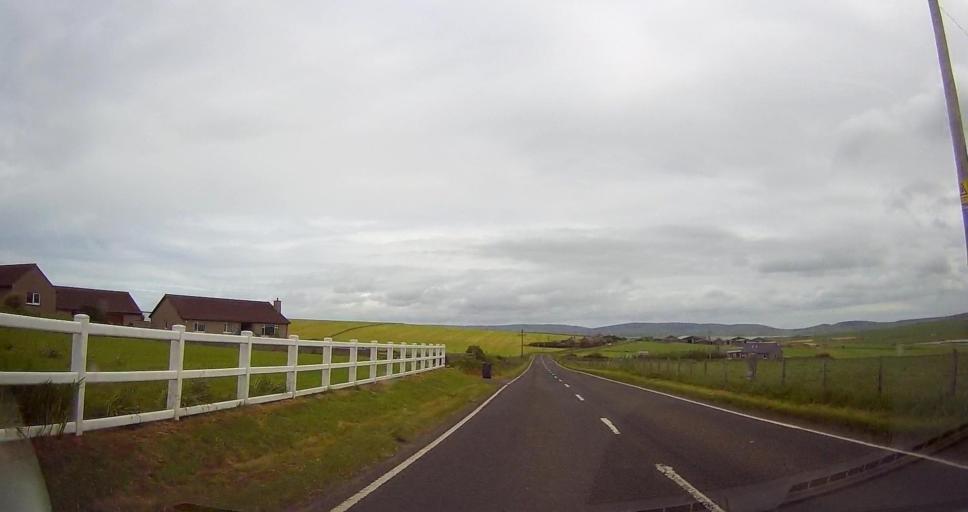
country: GB
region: Scotland
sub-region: Orkney Islands
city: Stromness
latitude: 58.9755
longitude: -3.2738
